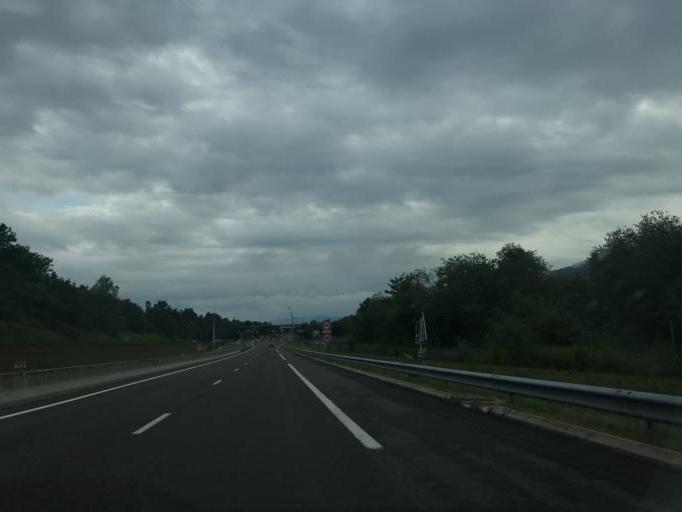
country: FR
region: Rhone-Alpes
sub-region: Departement de l'Ain
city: Groissiat
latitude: 46.2206
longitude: 5.6115
